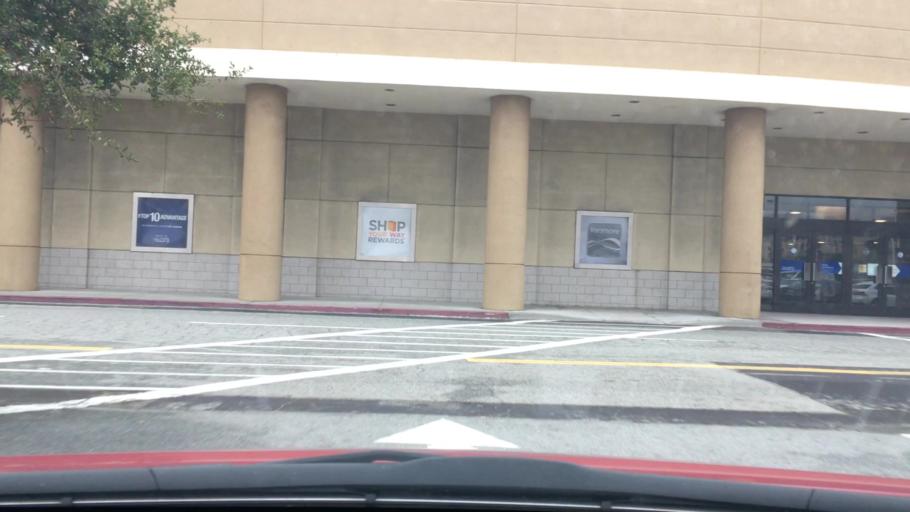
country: US
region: California
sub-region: San Mateo County
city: San Bruno
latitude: 37.6368
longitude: -122.4195
